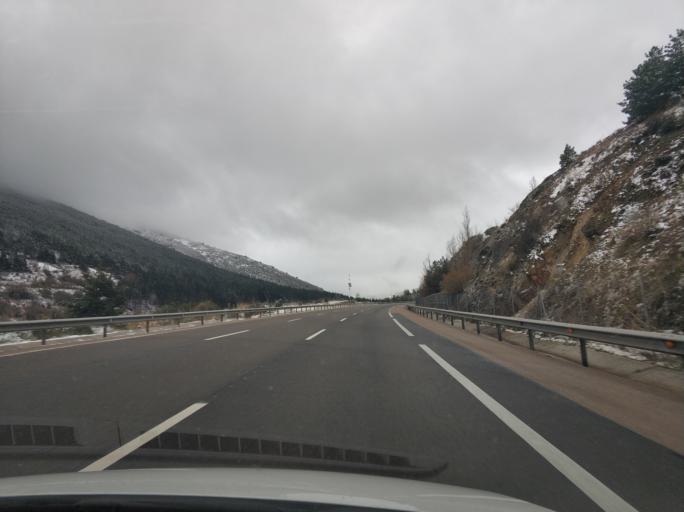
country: ES
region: Madrid
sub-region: Provincia de Madrid
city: Somosierra
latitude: 41.1707
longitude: -3.5823
